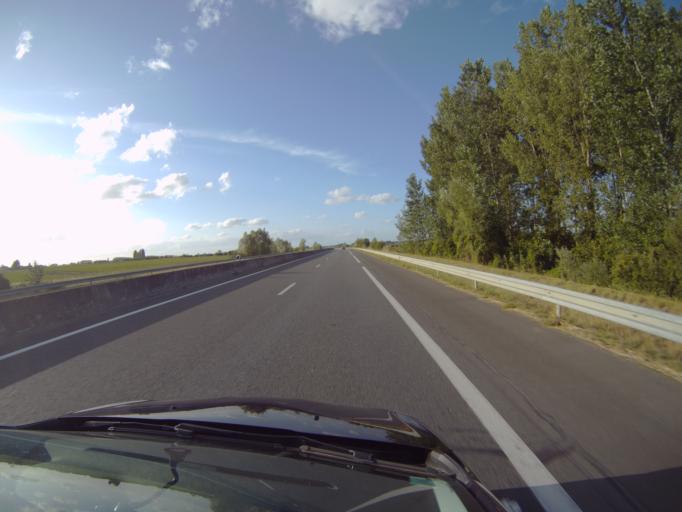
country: FR
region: Pays de la Loire
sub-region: Departement de Maine-et-Loire
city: Saint-Jean
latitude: 47.2618
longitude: -0.3341
